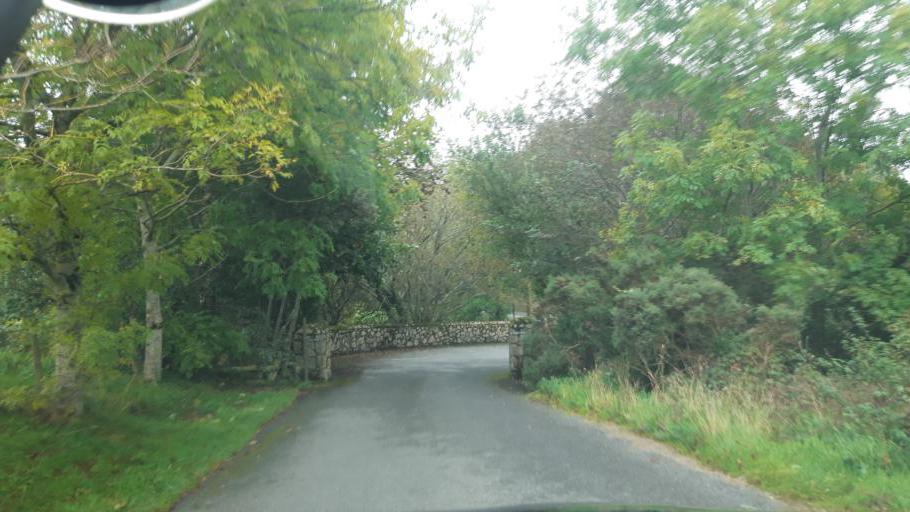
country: IE
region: Leinster
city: Sandyford
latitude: 53.2216
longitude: -6.2230
